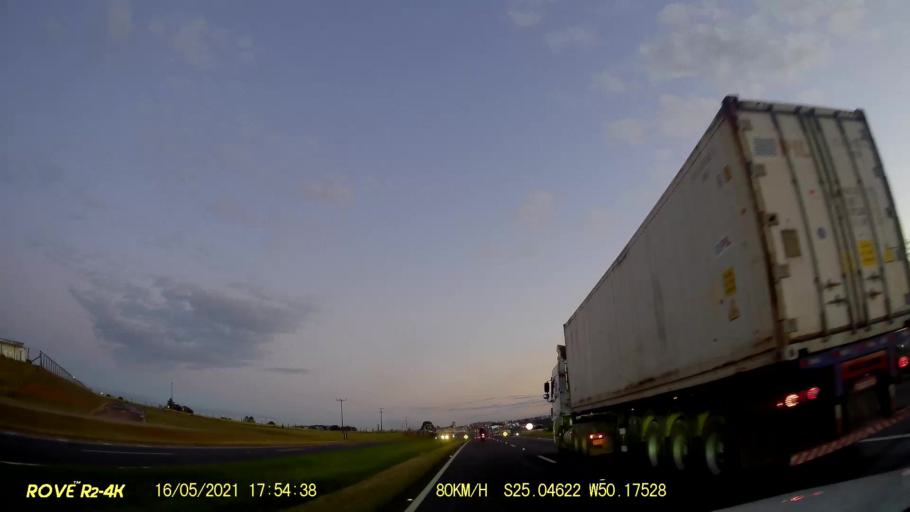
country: BR
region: Parana
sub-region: Ponta Grossa
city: Ponta Grossa
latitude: -25.0462
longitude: -50.1753
